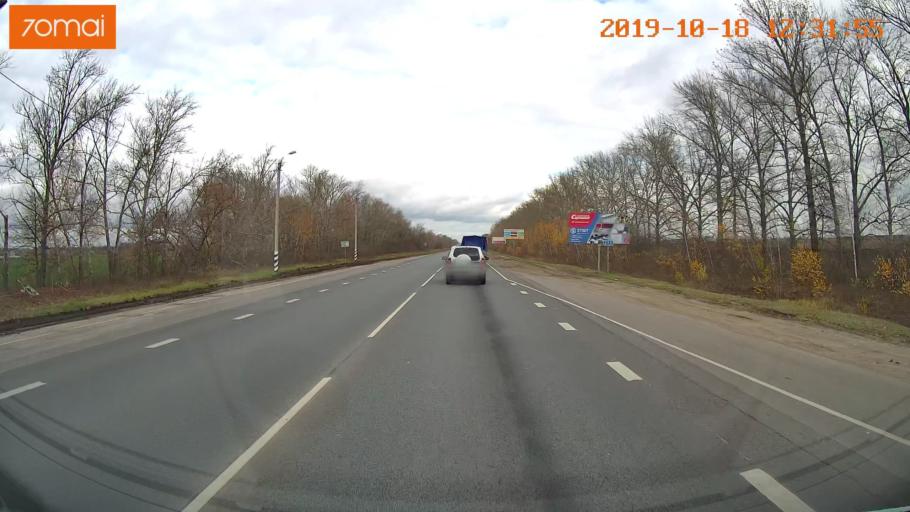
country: RU
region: Rjazan
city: Ryazan'
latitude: 54.5972
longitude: 39.6189
